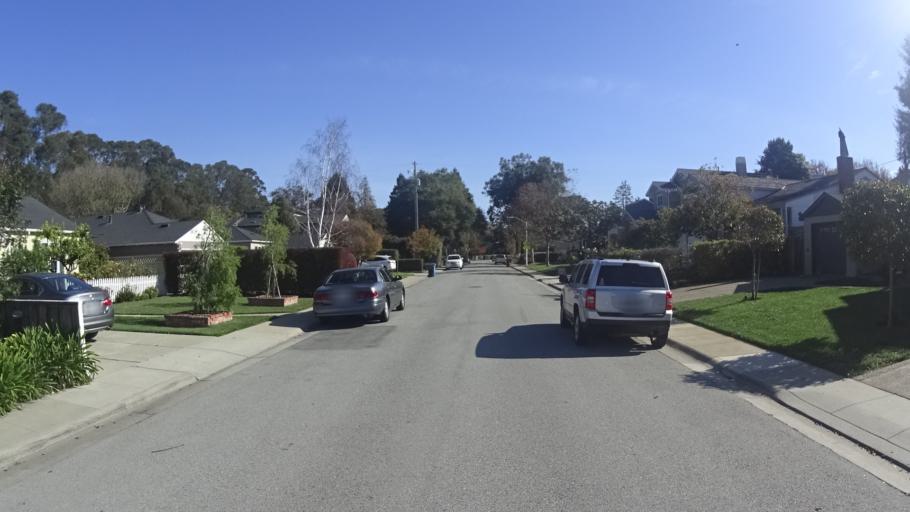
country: US
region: California
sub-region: San Mateo County
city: Burlingame
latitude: 37.5922
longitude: -122.3759
